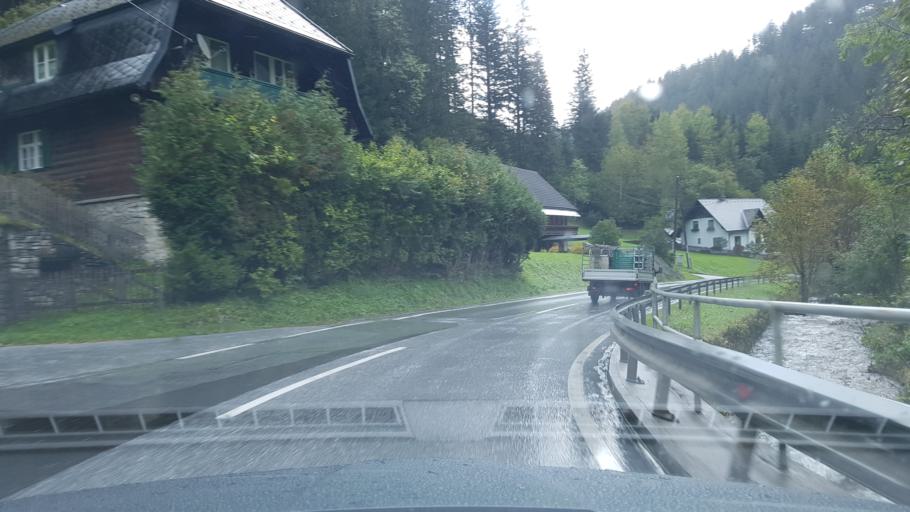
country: AT
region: Styria
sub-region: Politischer Bezirk Voitsberg
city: Salla
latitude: 47.1111
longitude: 14.9835
